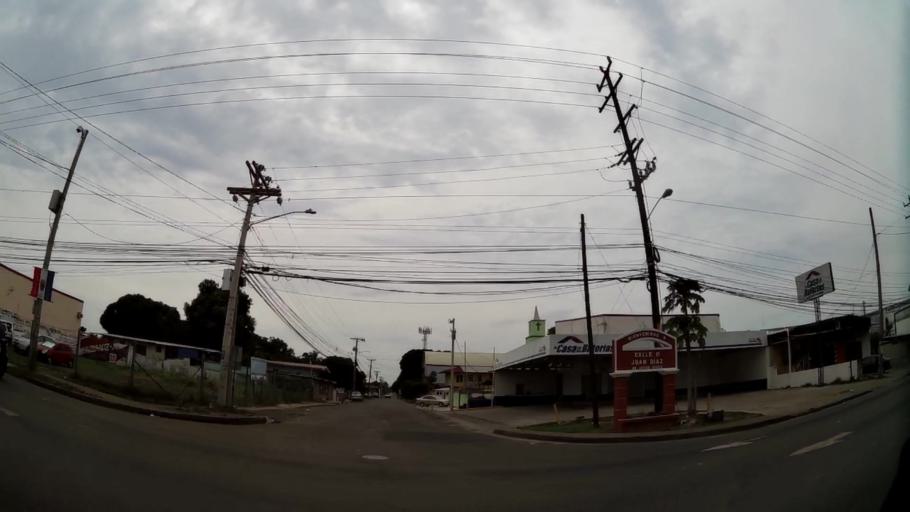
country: PA
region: Panama
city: San Miguelito
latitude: 9.0456
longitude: -79.4482
